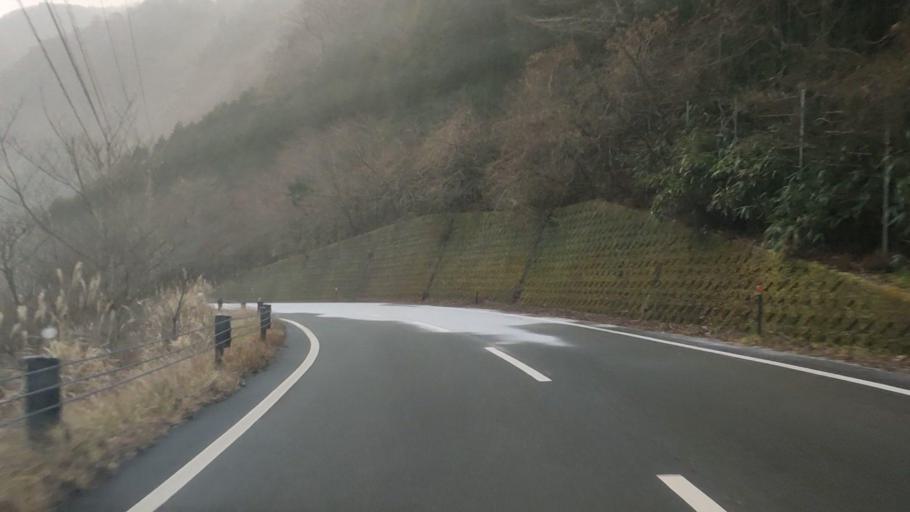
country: JP
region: Kumamoto
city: Matsubase
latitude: 32.5576
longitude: 130.9200
